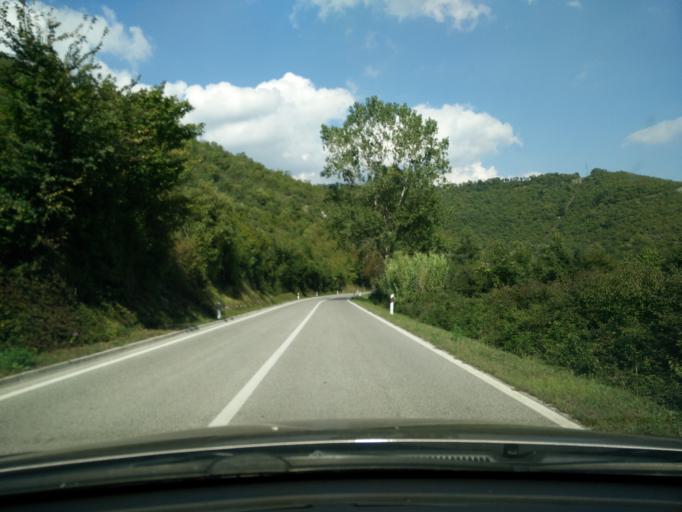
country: HR
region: Istarska
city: Buzet
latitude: 45.3931
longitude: 13.8978
